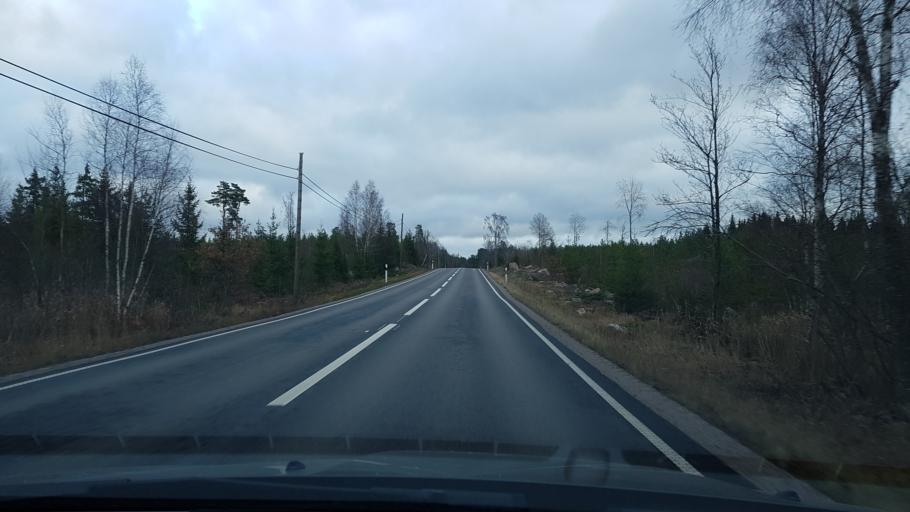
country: SE
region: Stockholm
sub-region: Norrtalje Kommun
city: Skanninge
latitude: 60.0175
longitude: 18.3728
